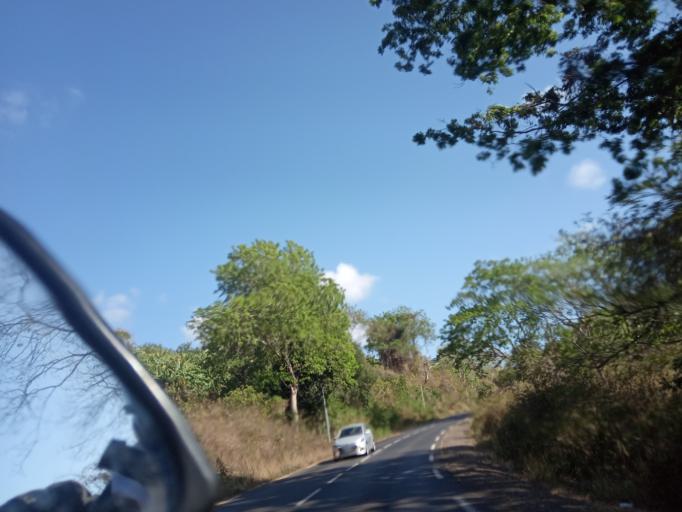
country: YT
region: Dembeni
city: Dembeni
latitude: -12.8708
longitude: 45.2074
